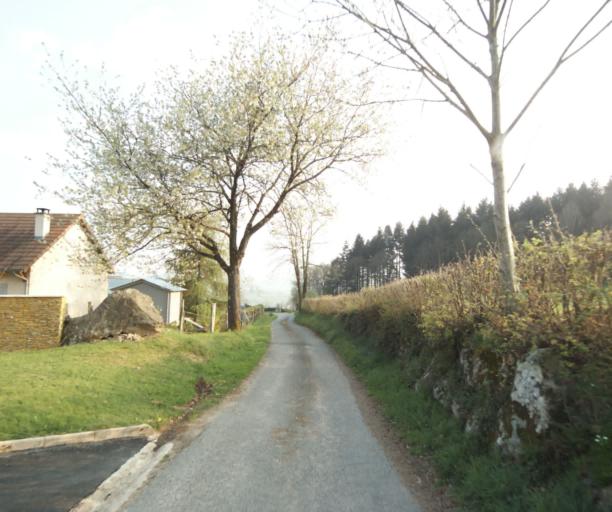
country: FR
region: Bourgogne
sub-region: Departement de Saone-et-Loire
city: Matour
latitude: 46.4348
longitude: 4.4594
